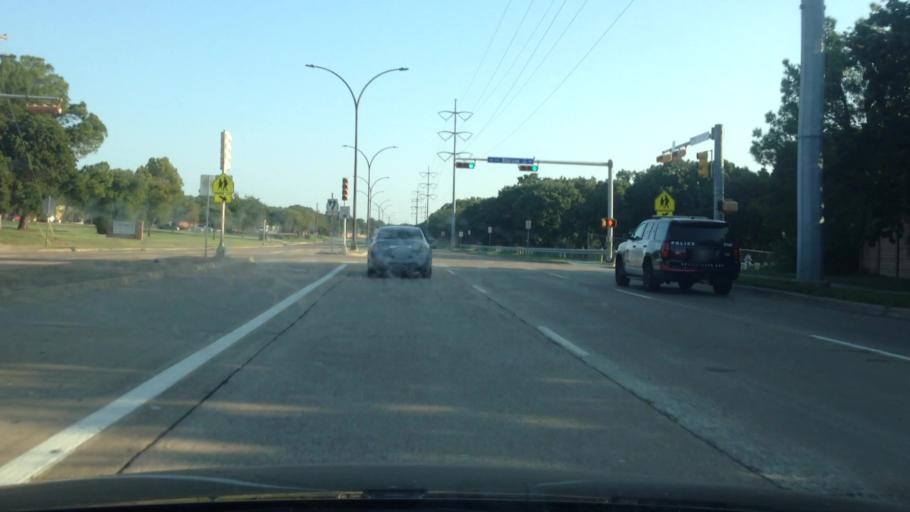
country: US
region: Texas
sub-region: Tarrant County
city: Dalworthington Gardens
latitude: 32.6976
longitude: -97.1904
